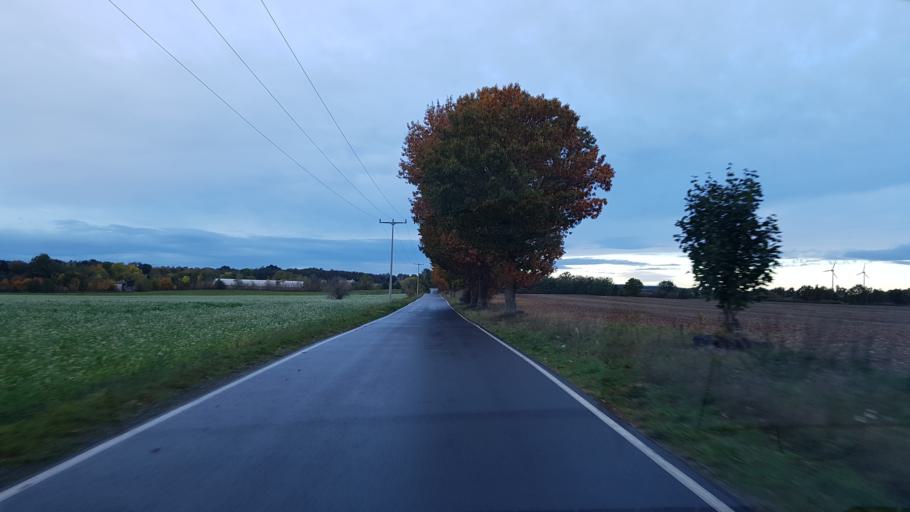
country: DE
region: Saxony
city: Belgern
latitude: 51.4598
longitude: 13.1407
